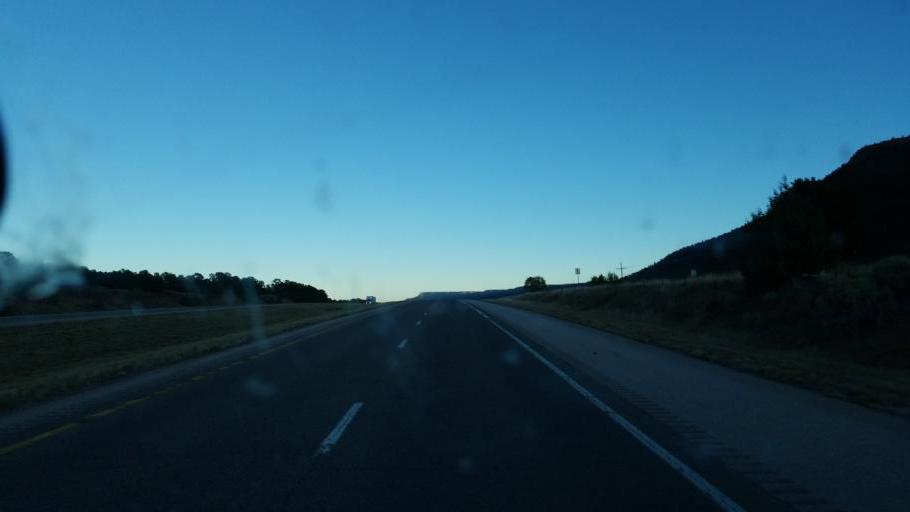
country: US
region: New Mexico
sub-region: San Miguel County
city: Pecos
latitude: 35.4754
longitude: -105.6596
